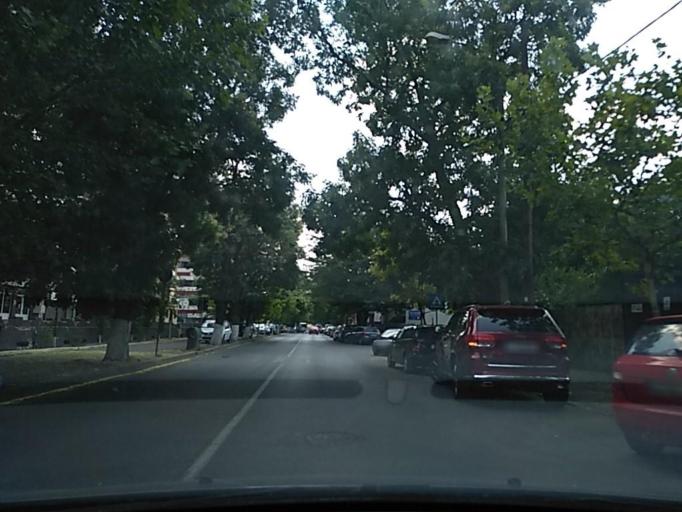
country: RO
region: Ilfov
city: Dobroesti
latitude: 44.4386
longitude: 26.1907
